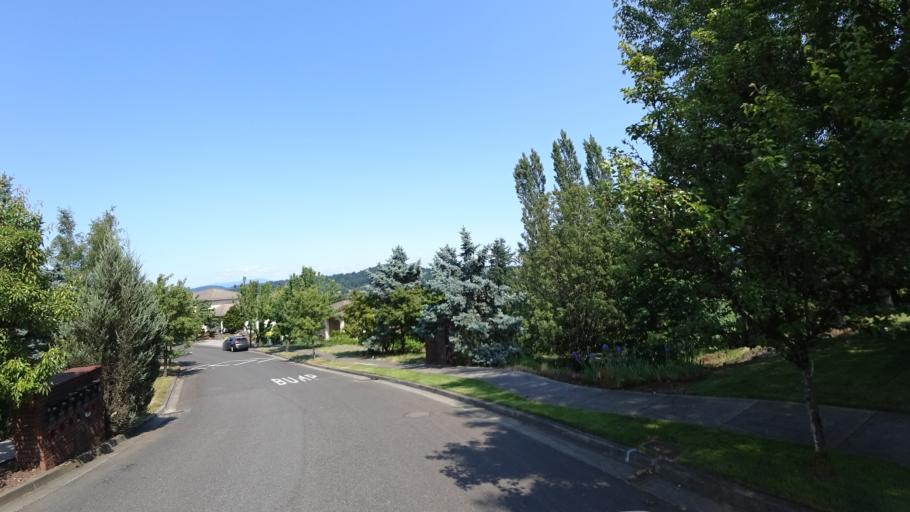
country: US
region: Oregon
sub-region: Clackamas County
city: Happy Valley
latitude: 45.4473
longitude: -122.5383
